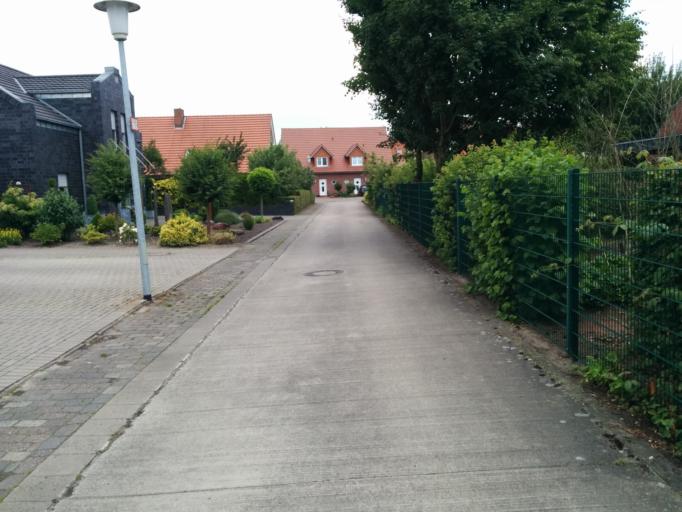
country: DE
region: Lower Saxony
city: Vechta
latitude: 52.7196
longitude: 8.2883
